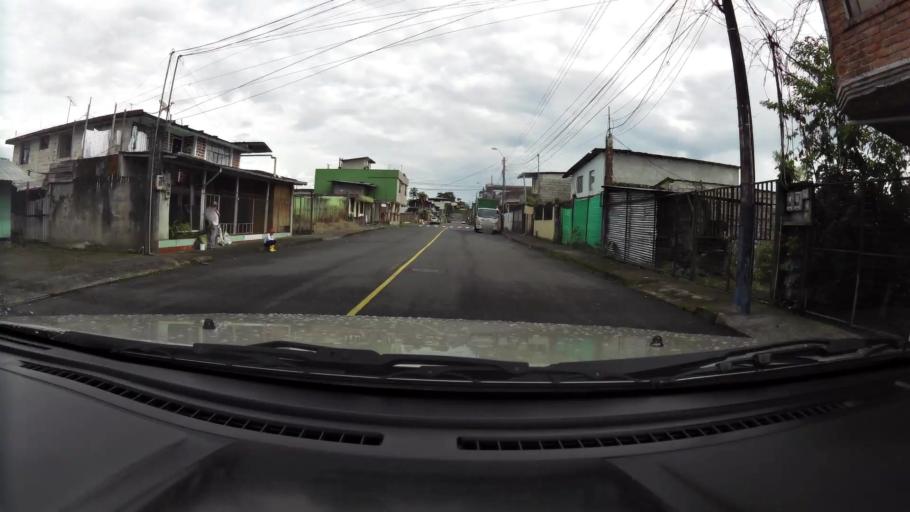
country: EC
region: Pastaza
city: Puyo
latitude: -1.4812
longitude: -77.9990
